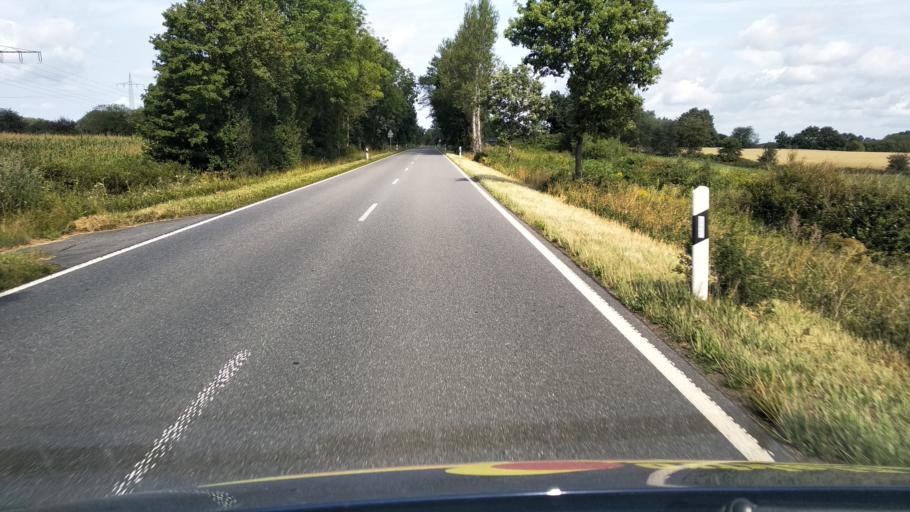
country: DE
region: Schleswig-Holstein
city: Geltorf
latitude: 54.4400
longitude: 9.6004
